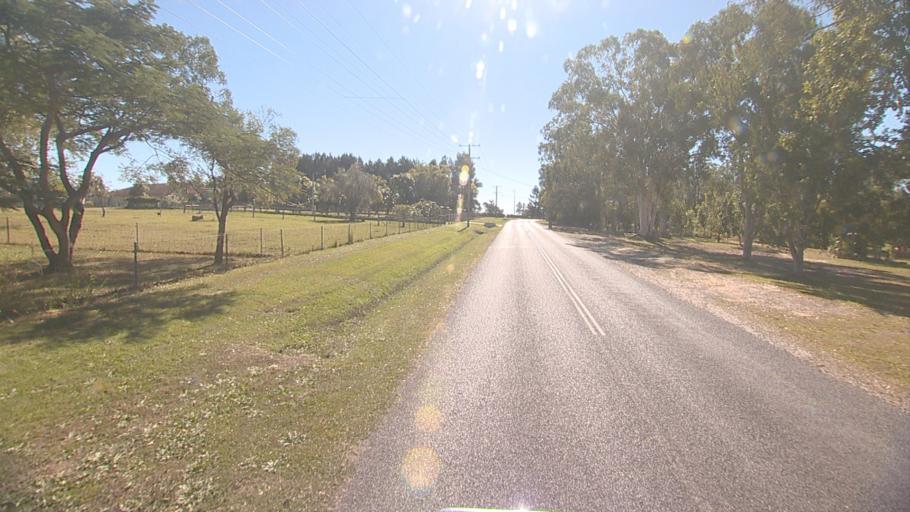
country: AU
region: Queensland
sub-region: Logan
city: Park Ridge South
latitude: -27.7084
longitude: 153.0584
